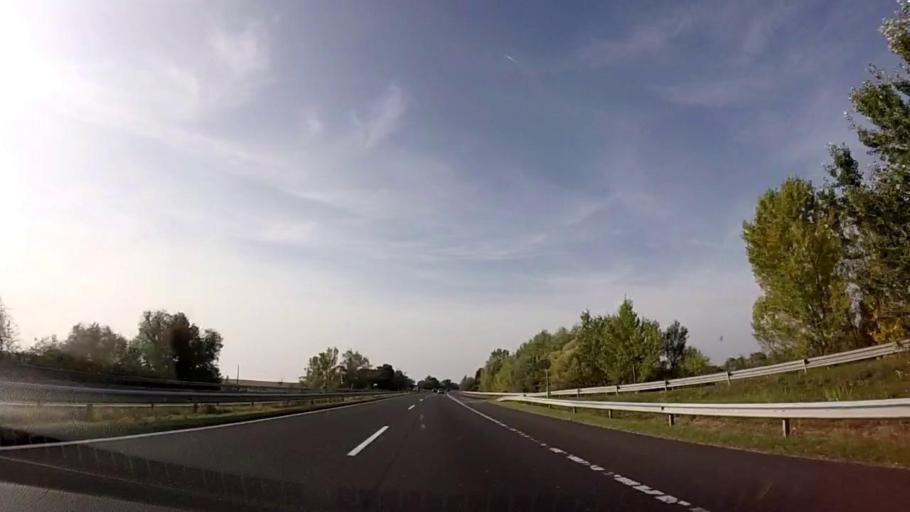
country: HU
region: Somogy
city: Balatonszabadi
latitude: 46.9293
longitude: 18.1355
